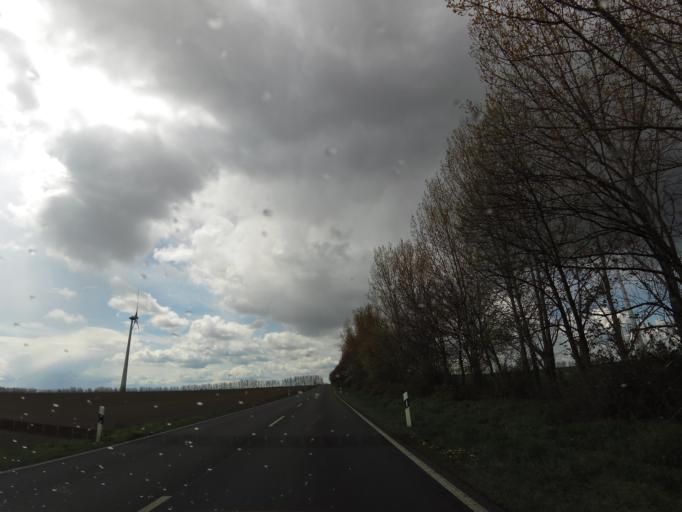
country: DE
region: Saxony-Anhalt
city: Klein Wanzleben
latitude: 52.0254
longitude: 11.3664
